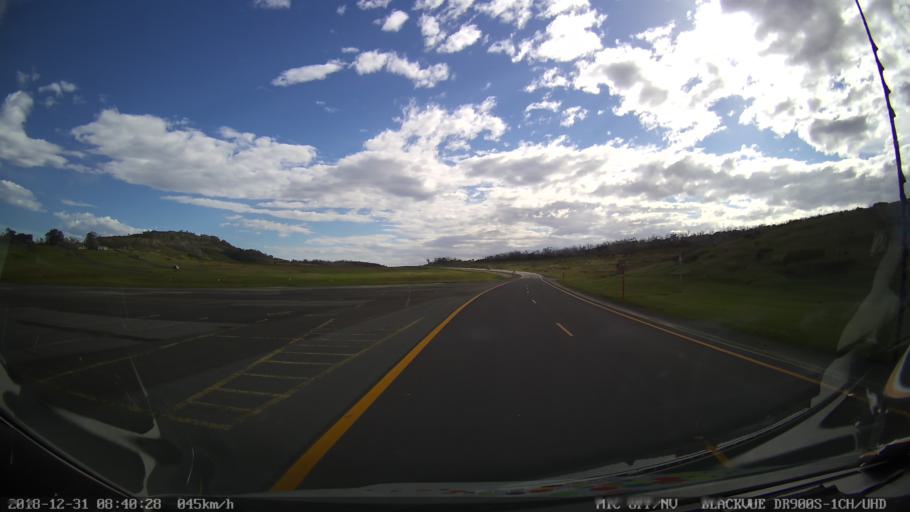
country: AU
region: New South Wales
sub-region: Snowy River
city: Jindabyne
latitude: -36.4047
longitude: 148.4137
